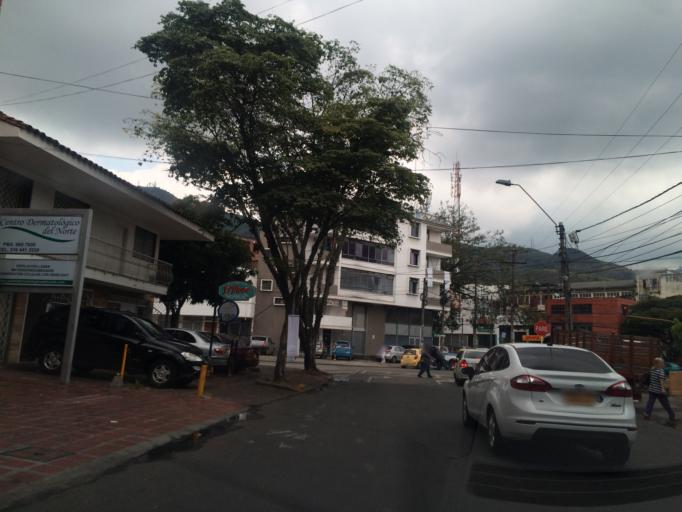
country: CO
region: Valle del Cauca
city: Cali
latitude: 3.4649
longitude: -76.5270
